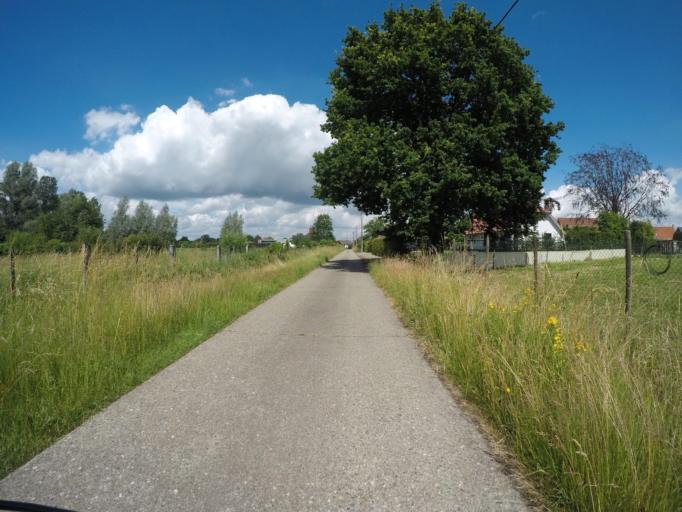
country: BE
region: Flanders
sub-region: Provincie Antwerpen
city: Brecht
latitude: 51.3497
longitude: 4.6595
